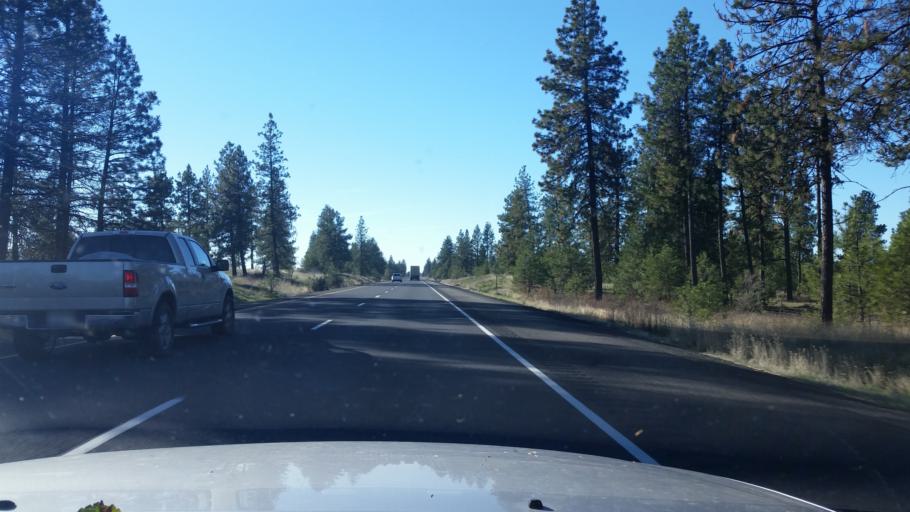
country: US
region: Washington
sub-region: Spokane County
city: Medical Lake
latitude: 47.4223
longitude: -117.8087
